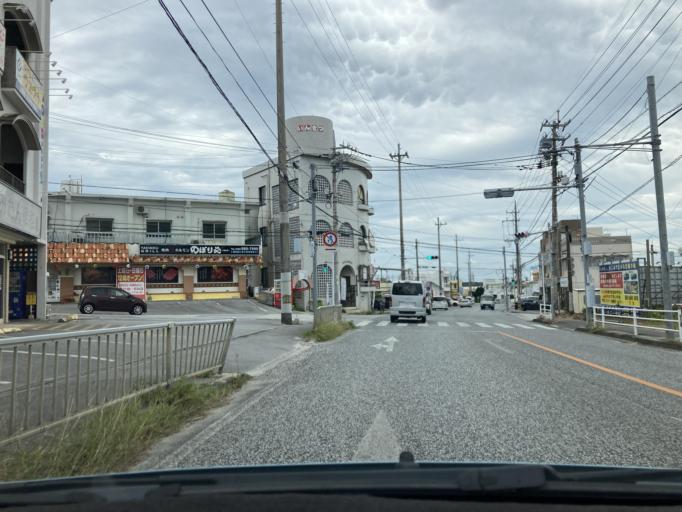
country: JP
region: Okinawa
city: Okinawa
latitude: 26.3824
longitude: 127.7487
